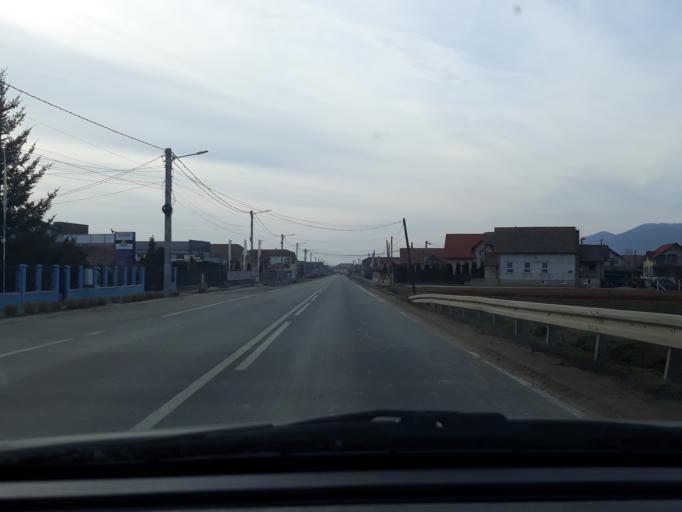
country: RO
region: Salaj
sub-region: Comuna Periceiu
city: Periceiu
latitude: 47.2255
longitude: 22.8733
